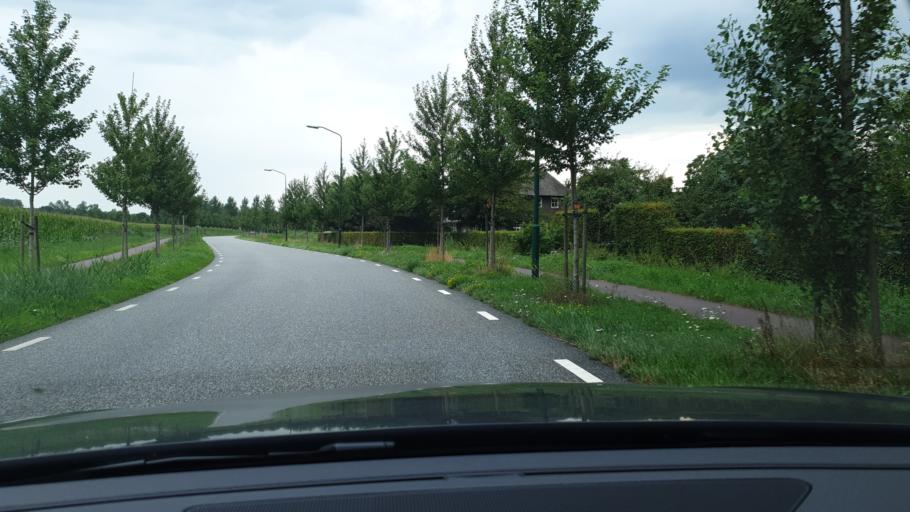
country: NL
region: North Brabant
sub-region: Gemeente Best
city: Best
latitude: 51.5388
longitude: 5.4202
